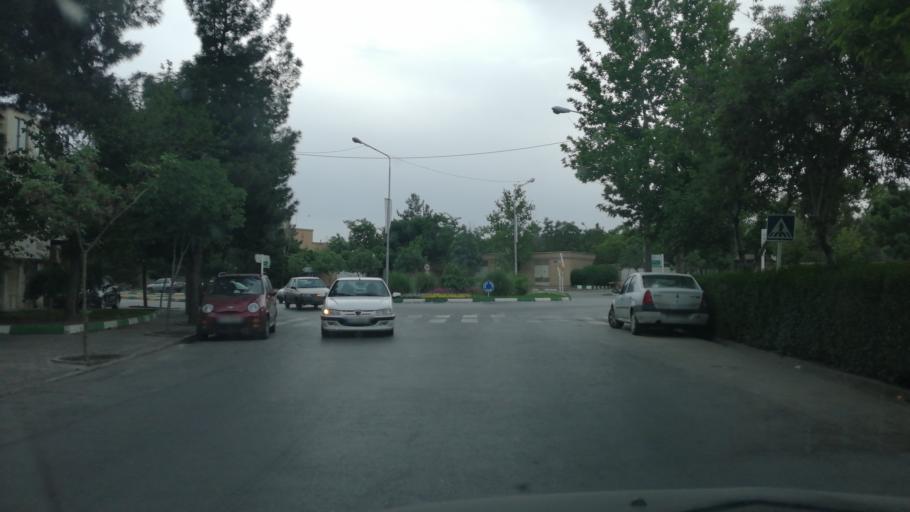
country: IR
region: Razavi Khorasan
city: Mashhad
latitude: 36.2866
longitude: 59.5822
